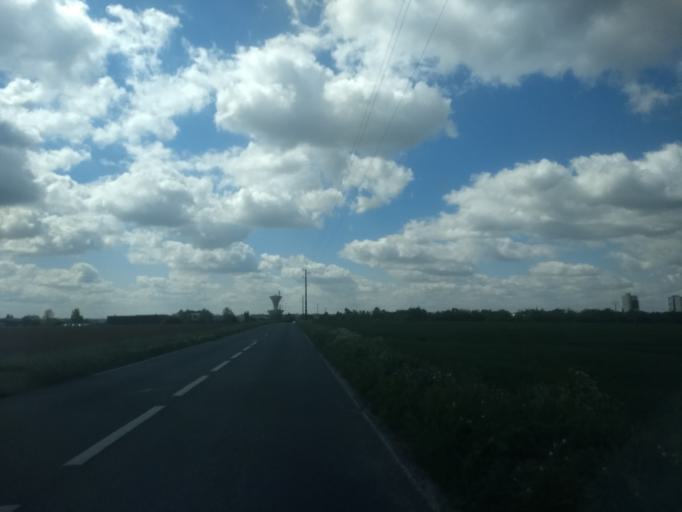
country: FR
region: Nord-Pas-de-Calais
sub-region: Departement du Pas-de-Calais
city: Saint-Laurent-Blangy
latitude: 50.3130
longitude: 2.8044
